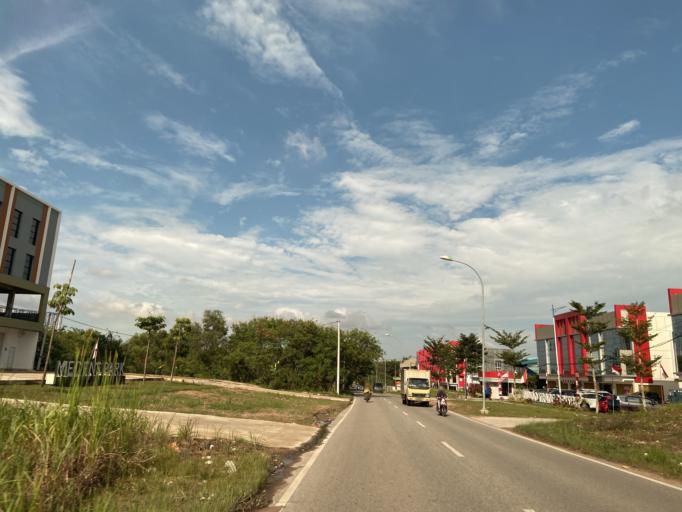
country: SG
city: Singapore
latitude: 1.1121
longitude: 104.0323
